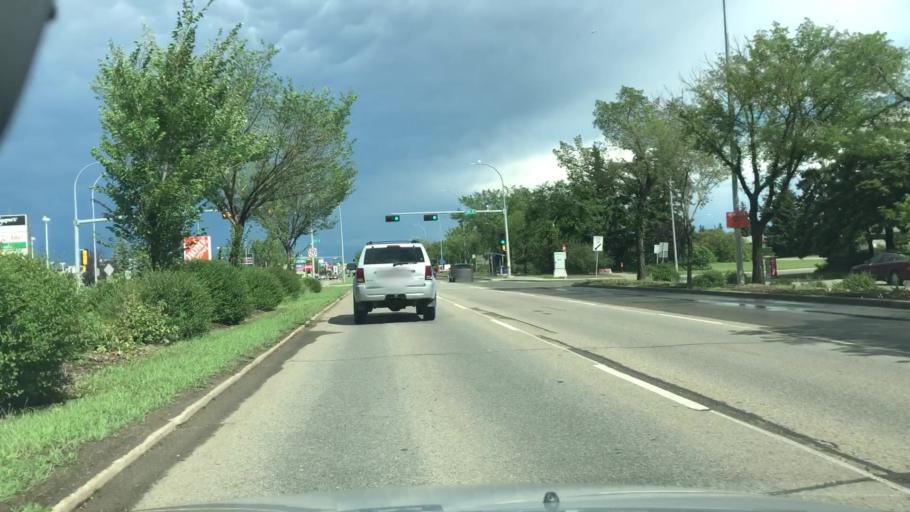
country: CA
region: Alberta
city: St. Albert
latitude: 53.5994
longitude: -113.5543
